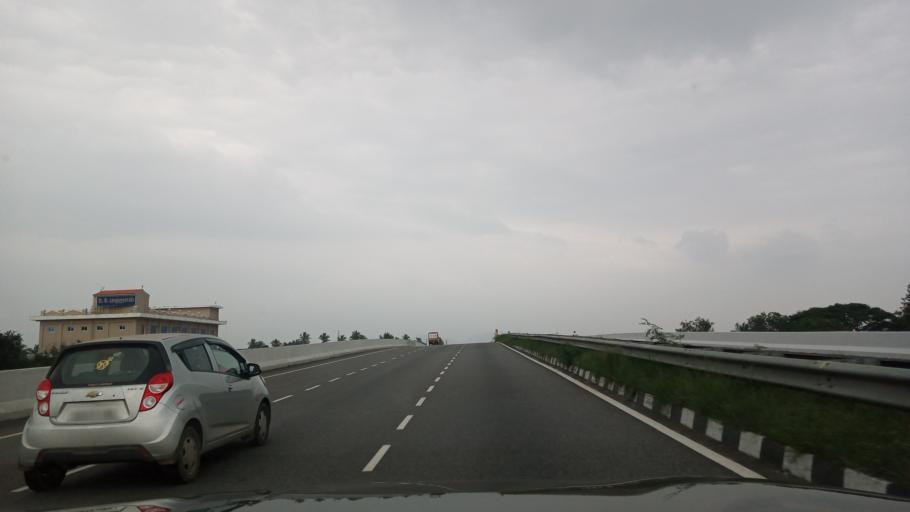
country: IN
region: Tamil Nadu
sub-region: Vellore
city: Vellore
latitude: 12.9150
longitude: 79.0652
